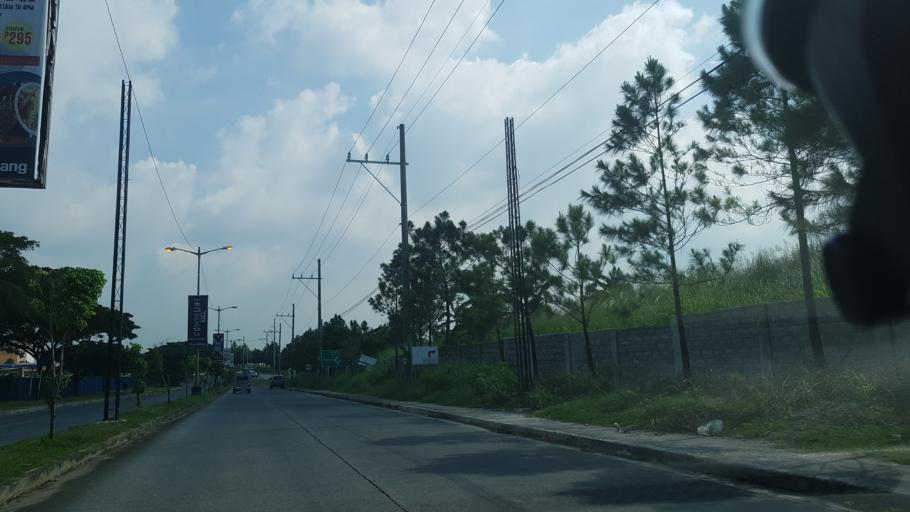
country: PH
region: Calabarzon
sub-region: Province of Laguna
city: San Pedro
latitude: 14.3717
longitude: 121.0112
